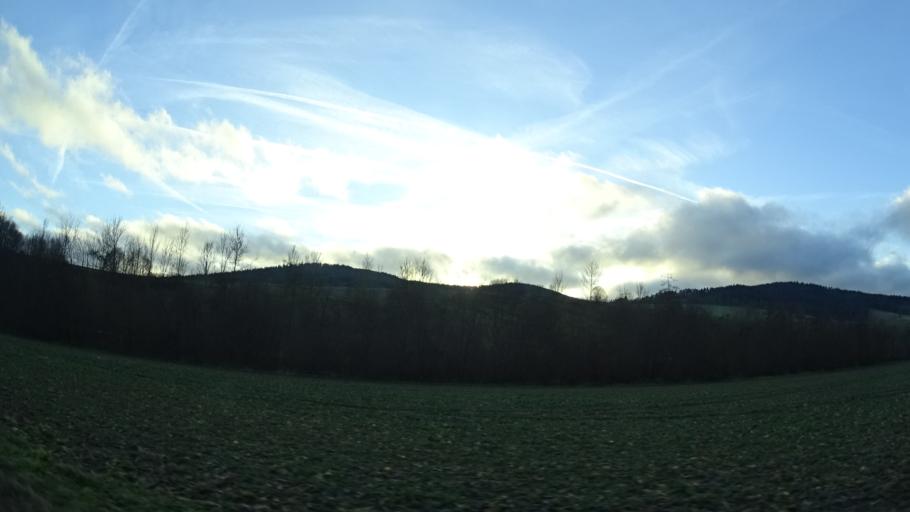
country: DE
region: Thuringia
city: Rudolstadt
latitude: 50.7500
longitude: 11.3141
